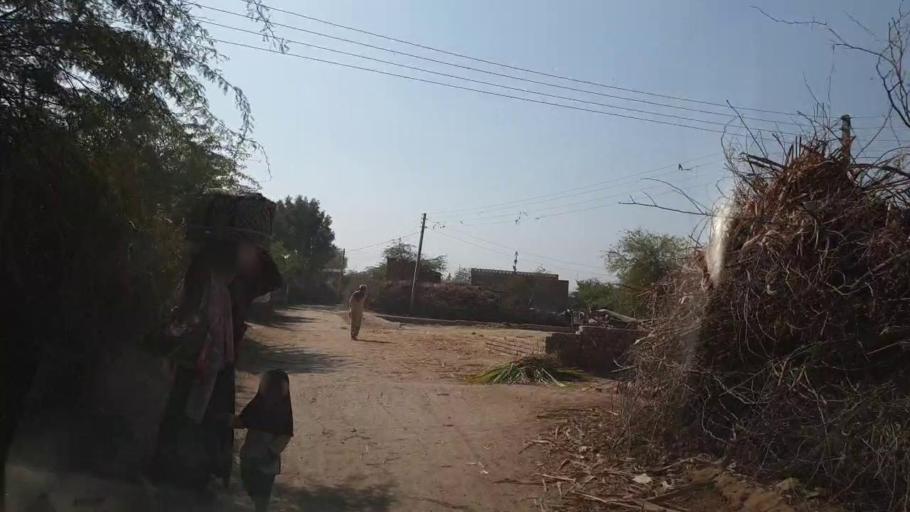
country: PK
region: Sindh
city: Matiari
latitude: 25.5160
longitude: 68.4607
